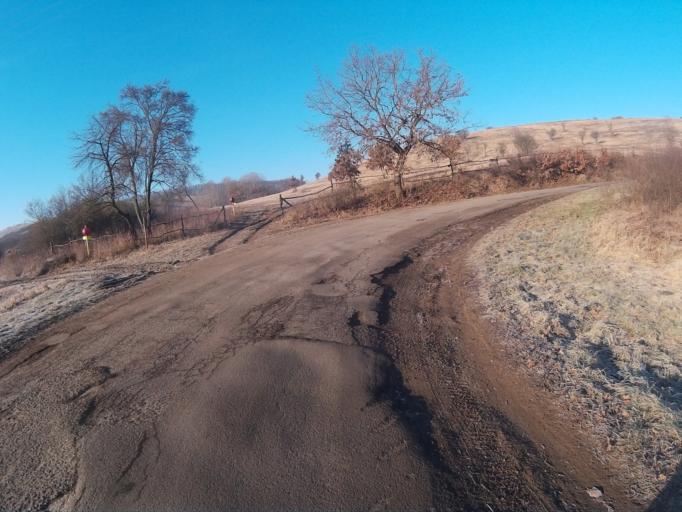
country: HU
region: Borsod-Abauj-Zemplen
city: Putnok
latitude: 48.3657
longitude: 20.4271
